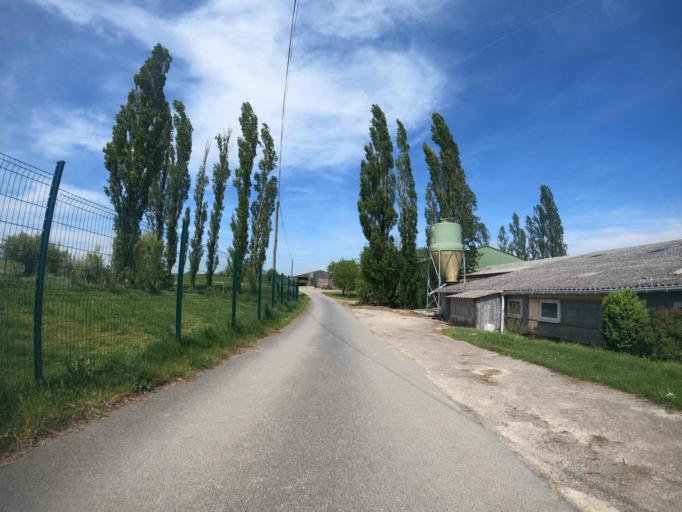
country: FR
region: Poitou-Charentes
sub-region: Departement des Deux-Sevres
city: Secondigny
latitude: 46.6468
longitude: -0.4924
